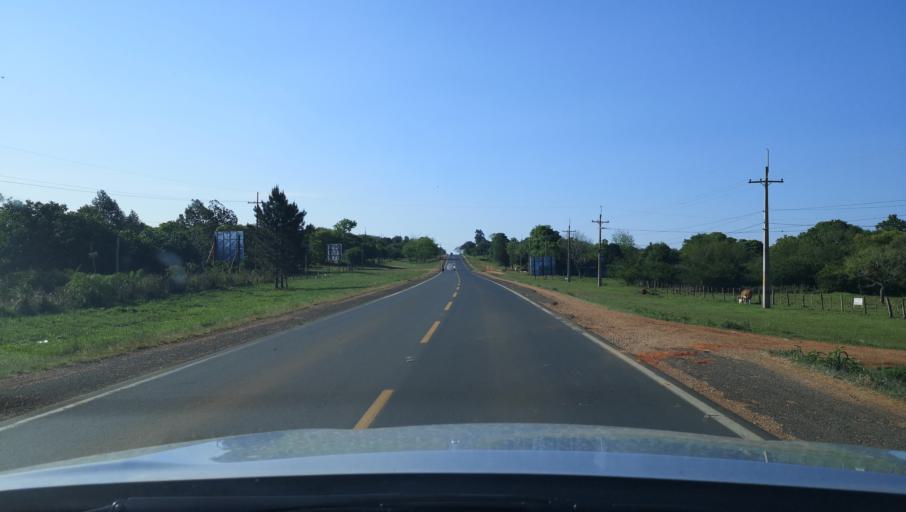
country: PY
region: Misiones
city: Santa Maria
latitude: -26.8683
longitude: -57.0328
